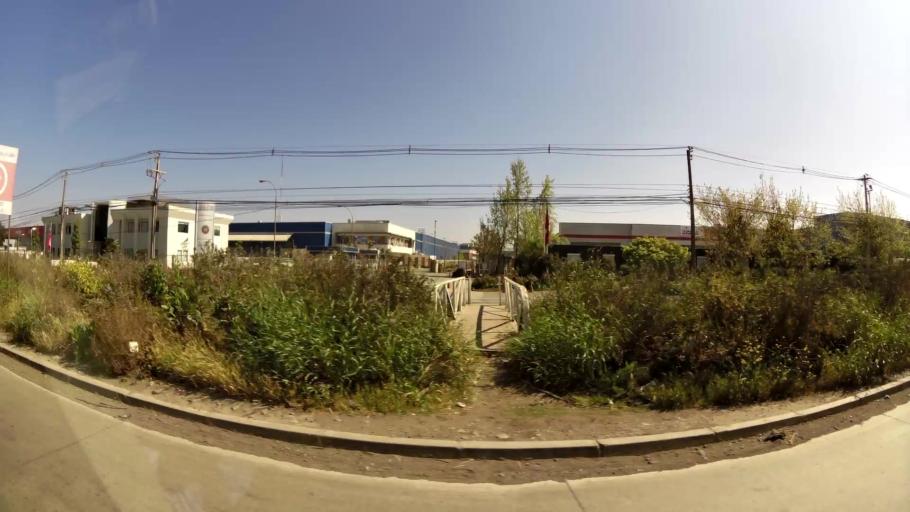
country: CL
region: Santiago Metropolitan
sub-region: Provincia de Chacabuco
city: Chicureo Abajo
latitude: -33.3170
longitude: -70.7307
